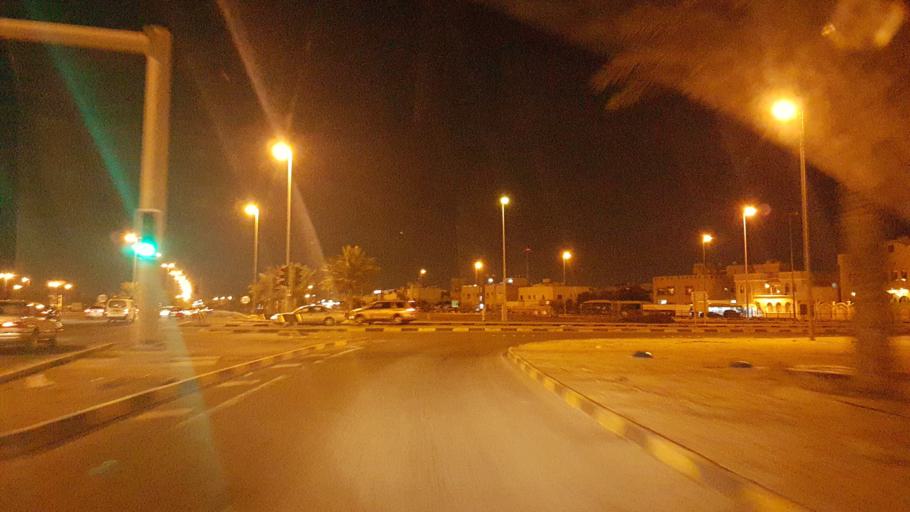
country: BH
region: Muharraq
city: Al Hadd
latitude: 26.2454
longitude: 50.6583
